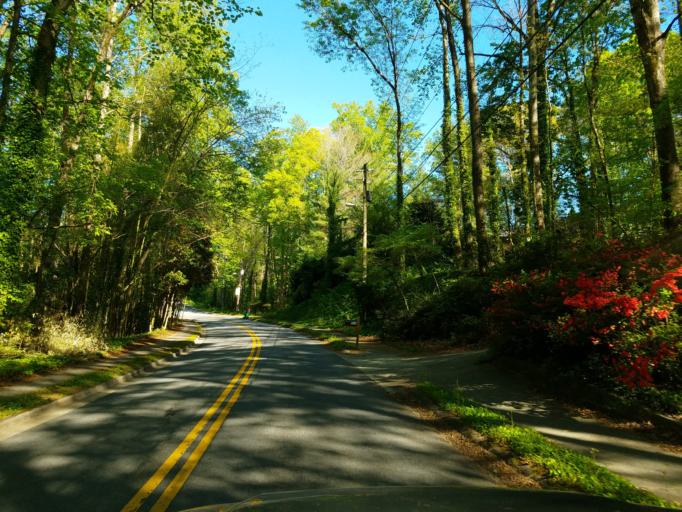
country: US
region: Georgia
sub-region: Cobb County
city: Smyrna
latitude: 33.8541
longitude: -84.5271
